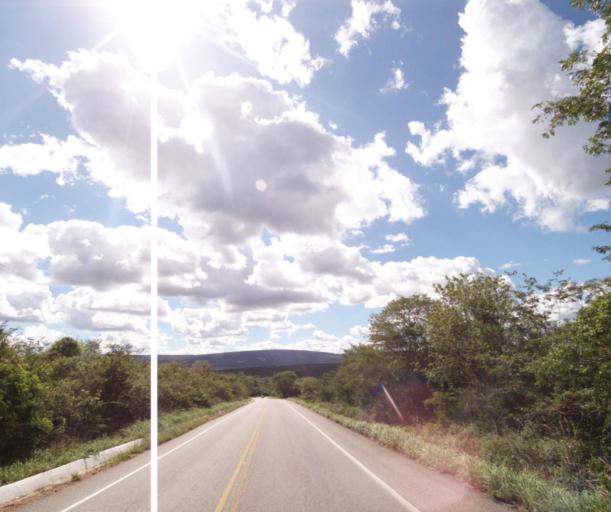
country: BR
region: Bahia
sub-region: Caetite
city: Caetite
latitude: -14.1306
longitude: -42.3951
